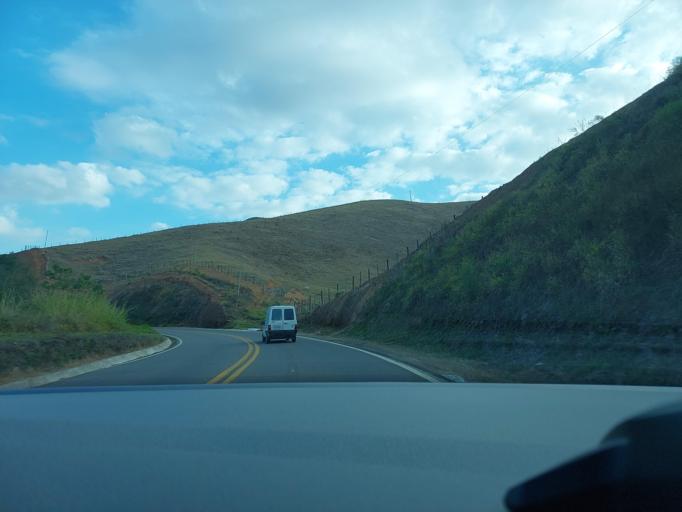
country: BR
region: Minas Gerais
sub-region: Muriae
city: Muriae
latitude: -21.0606
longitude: -42.5024
